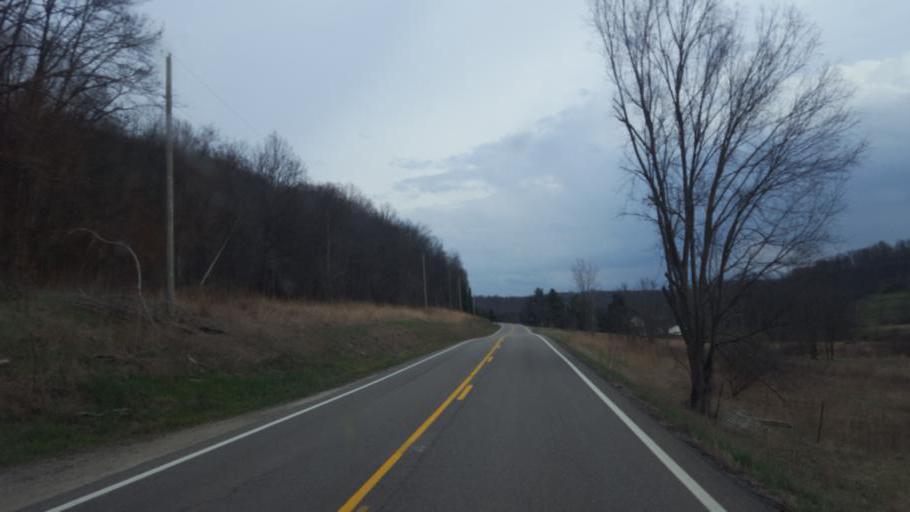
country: US
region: Ohio
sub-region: Guernsey County
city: Mantua
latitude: 40.1245
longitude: -81.7726
